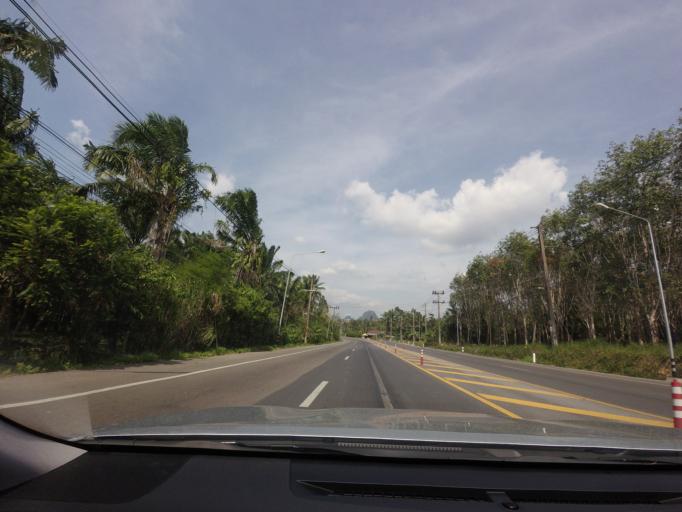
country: TH
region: Phangnga
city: Ban Ao Nang
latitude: 8.0886
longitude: 98.8092
